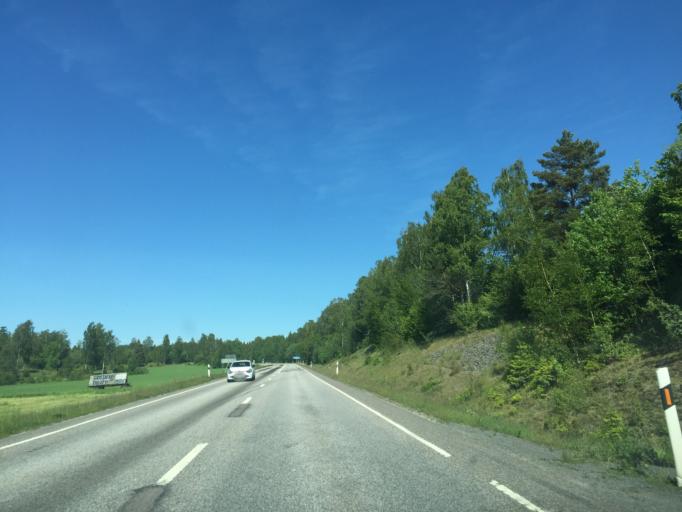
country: SE
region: OEstergoetland
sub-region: Motala Kommun
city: Ryd
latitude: 58.6526
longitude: 14.9587
